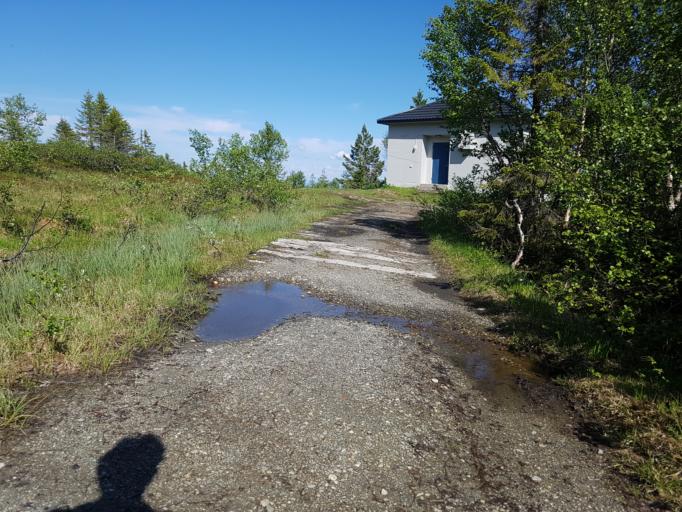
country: NO
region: Sor-Trondelag
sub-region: Trondheim
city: Trondheim
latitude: 63.4212
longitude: 10.2597
